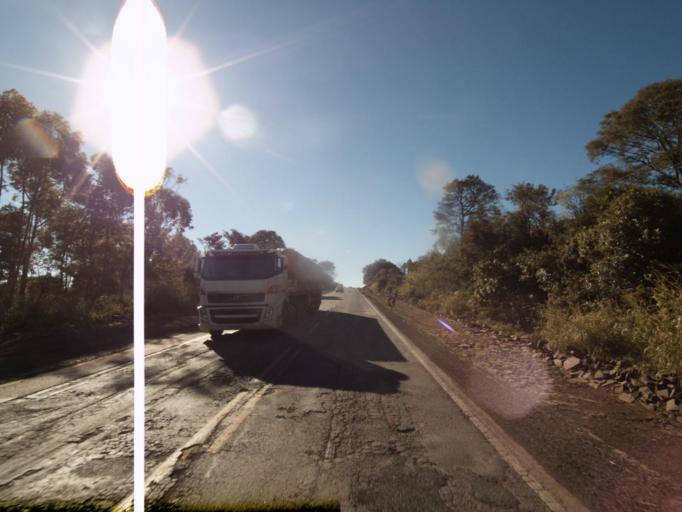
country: AR
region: Misiones
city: Bernardo de Irigoyen
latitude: -26.6536
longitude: -53.5176
